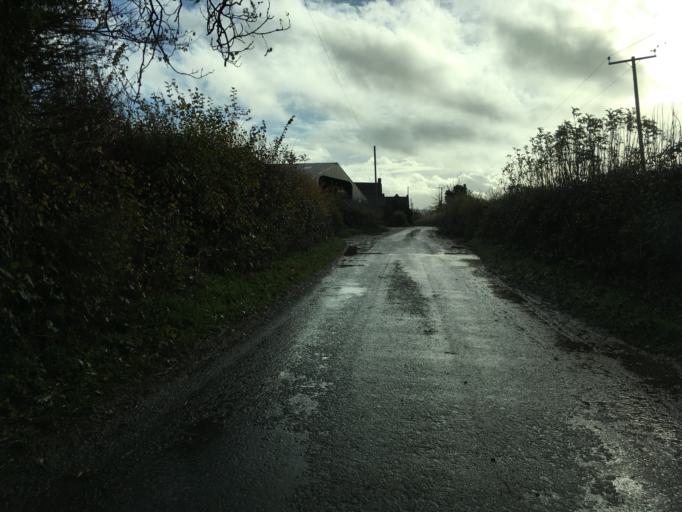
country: GB
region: England
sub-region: South Gloucestershire
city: Hinton
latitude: 51.4759
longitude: -2.4083
